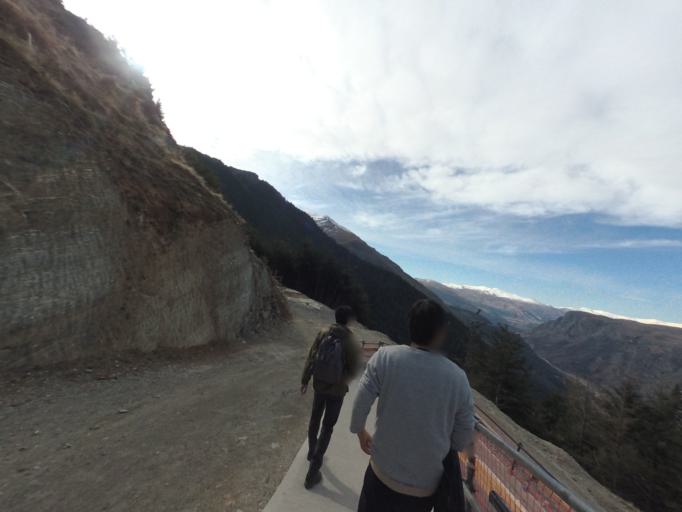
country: NZ
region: Otago
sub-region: Queenstown-Lakes District
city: Queenstown
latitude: -45.0257
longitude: 168.6497
